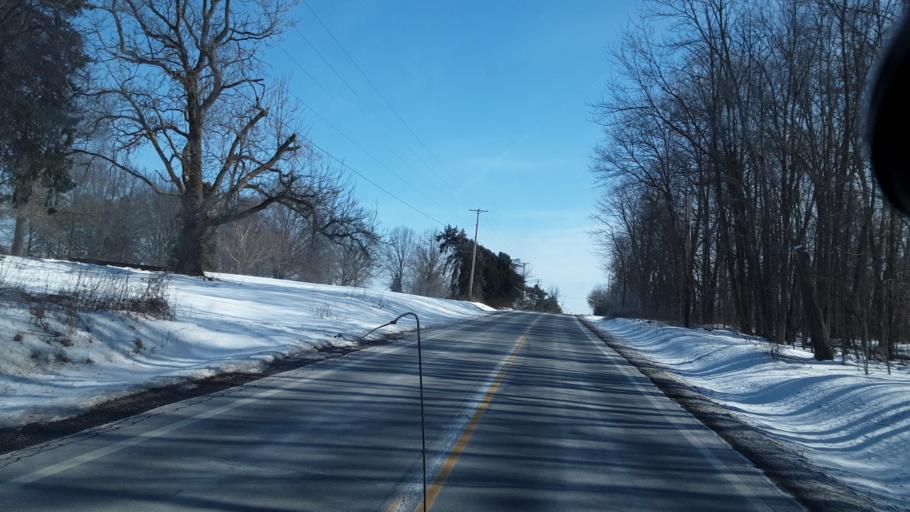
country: US
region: Ohio
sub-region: Mahoning County
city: Sebring
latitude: 40.9543
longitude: -80.9601
